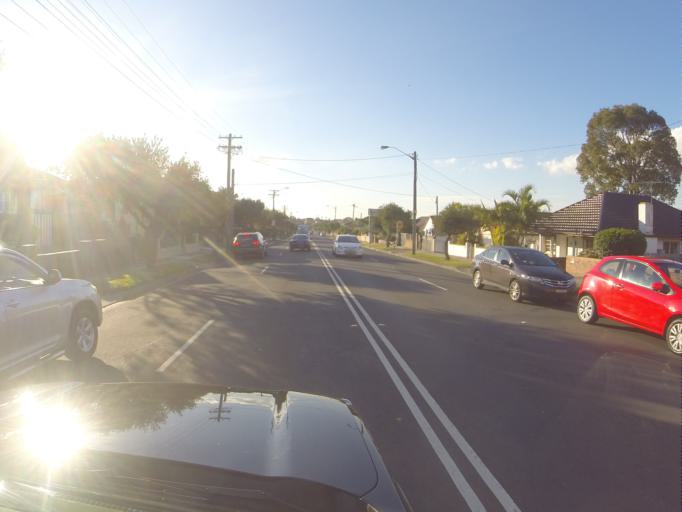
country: AU
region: New South Wales
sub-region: Rockdale
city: Bexley North
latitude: -33.9267
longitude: 151.1087
